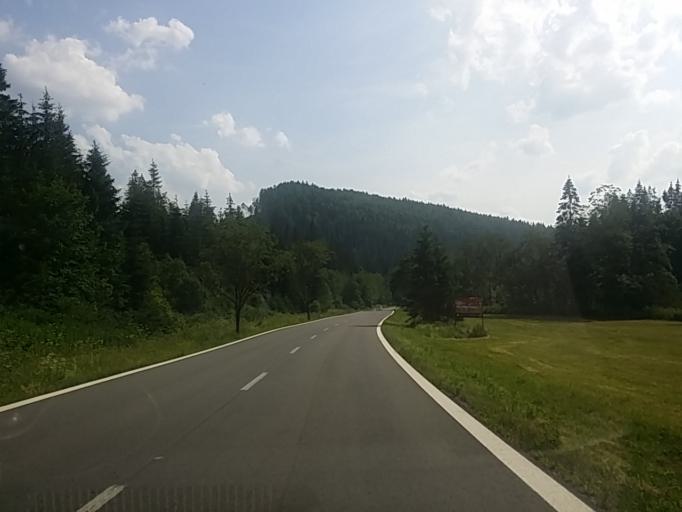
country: SK
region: Banskobystricky
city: Revuca
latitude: 48.8223
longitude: 20.1466
